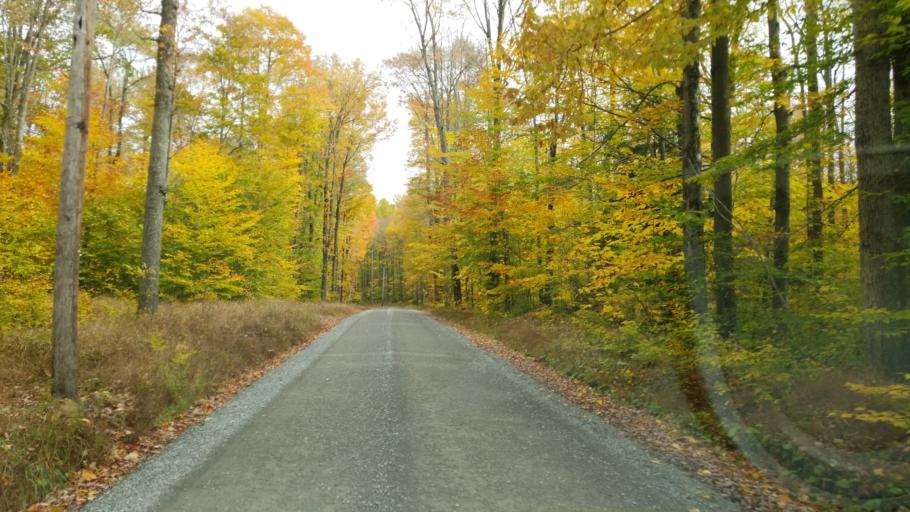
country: US
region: Pennsylvania
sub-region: Clearfield County
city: Clearfield
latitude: 41.1962
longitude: -78.3920
